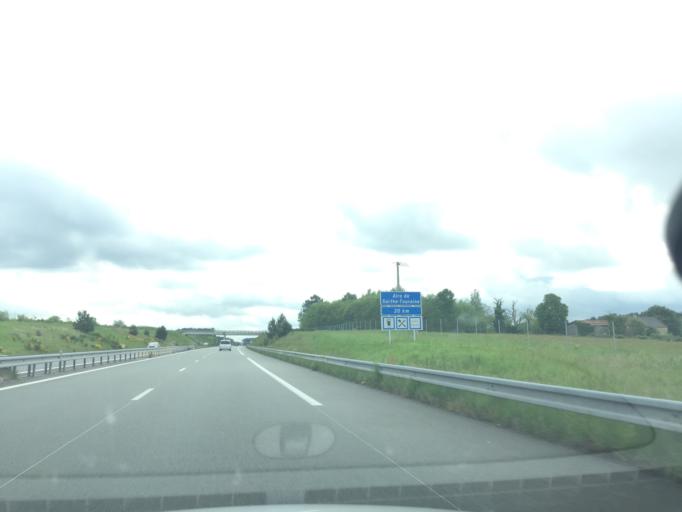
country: FR
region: Pays de la Loire
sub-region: Departement de la Sarthe
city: Mayet
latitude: 47.7704
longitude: 0.3139
